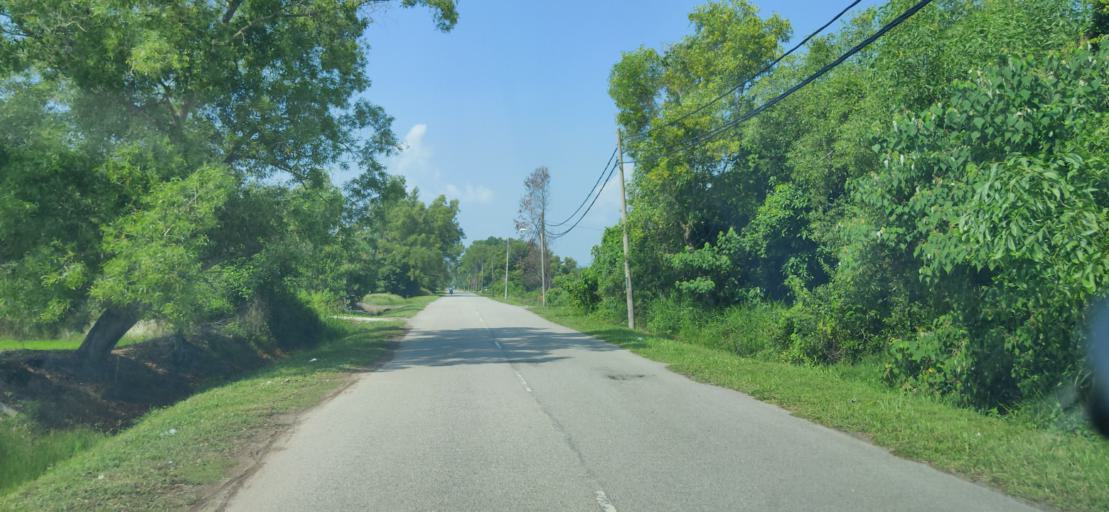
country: MY
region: Kedah
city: Sungai Petani
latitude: 5.6726
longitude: 100.4620
